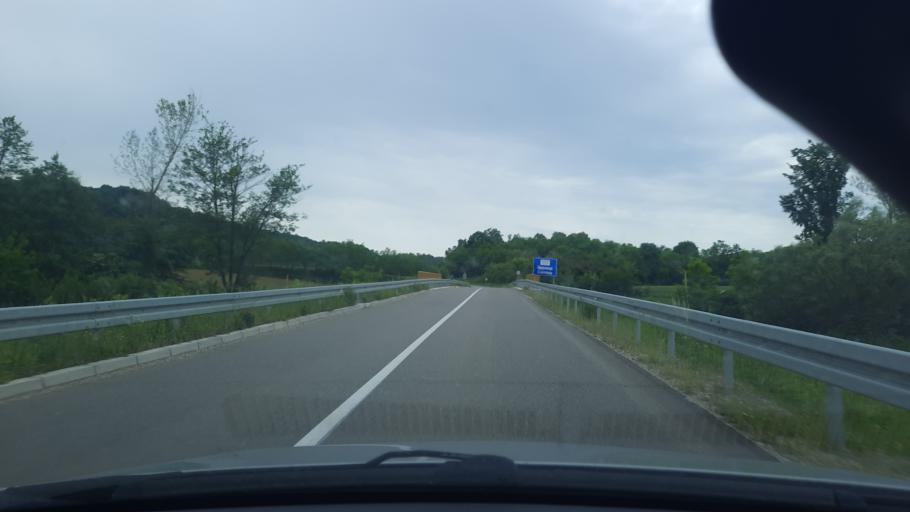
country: RS
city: Bukor
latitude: 44.5268
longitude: 19.5144
